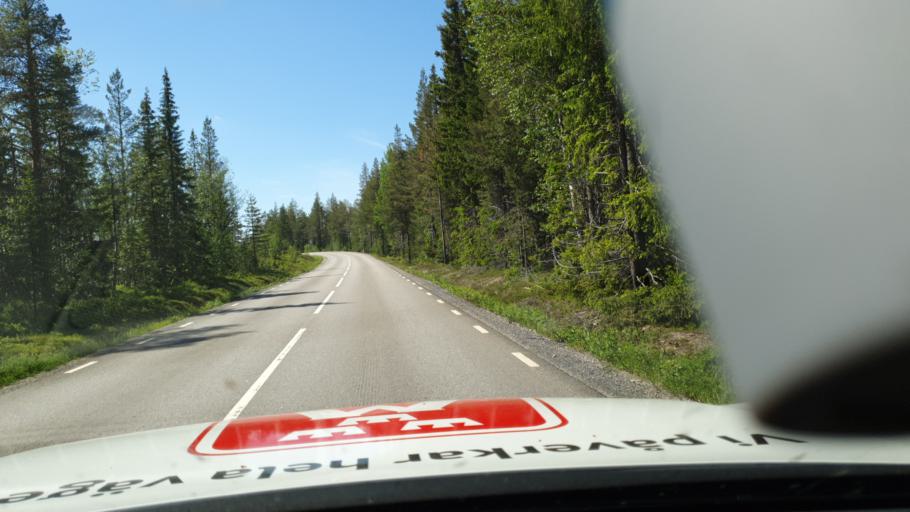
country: SE
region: Jaemtland
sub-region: Harjedalens Kommun
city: Sveg
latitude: 62.1054
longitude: 13.4443
